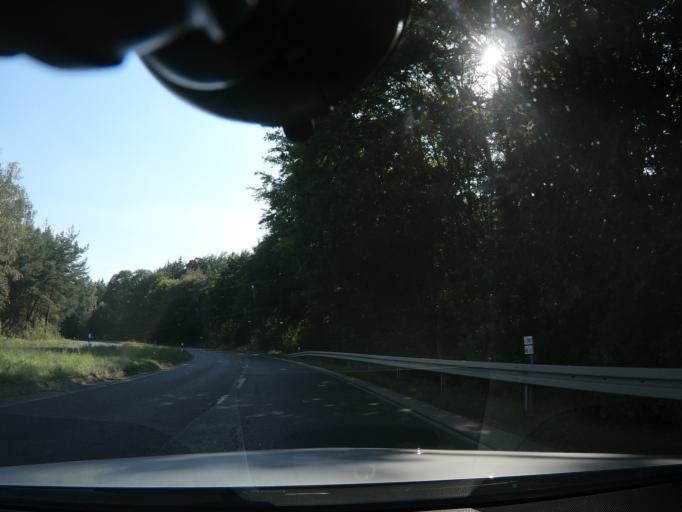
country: DE
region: Hesse
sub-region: Regierungsbezirk Giessen
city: Marburg an der Lahn
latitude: 50.8105
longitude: 8.8048
